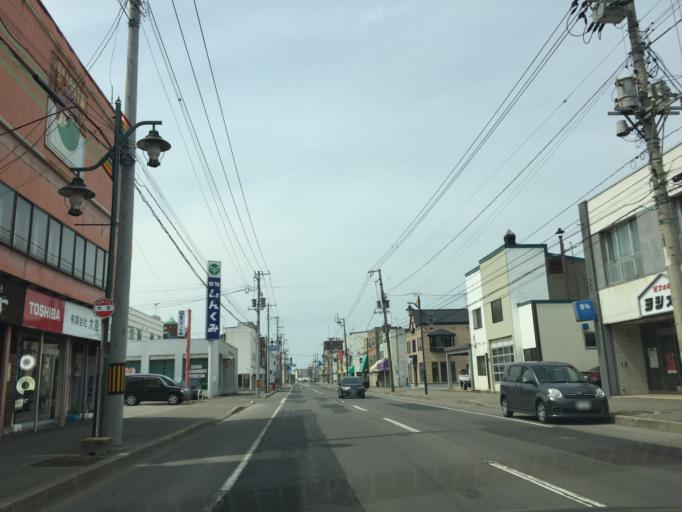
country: JP
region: Hokkaido
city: Akabira
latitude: 43.5541
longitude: 142.0518
